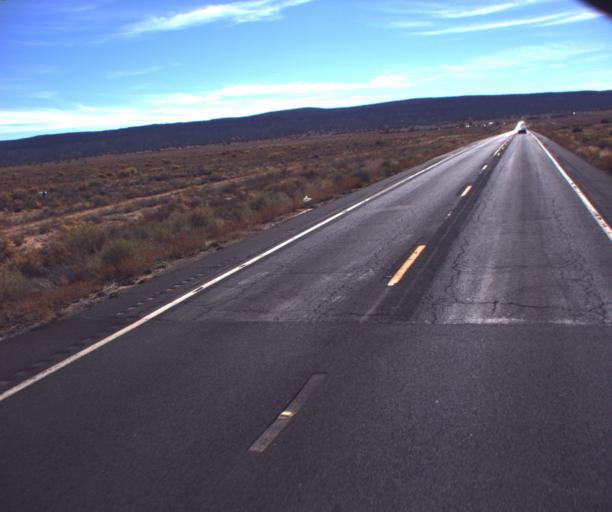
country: US
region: Arizona
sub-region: Coconino County
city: Kaibito
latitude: 36.4722
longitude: -110.6984
